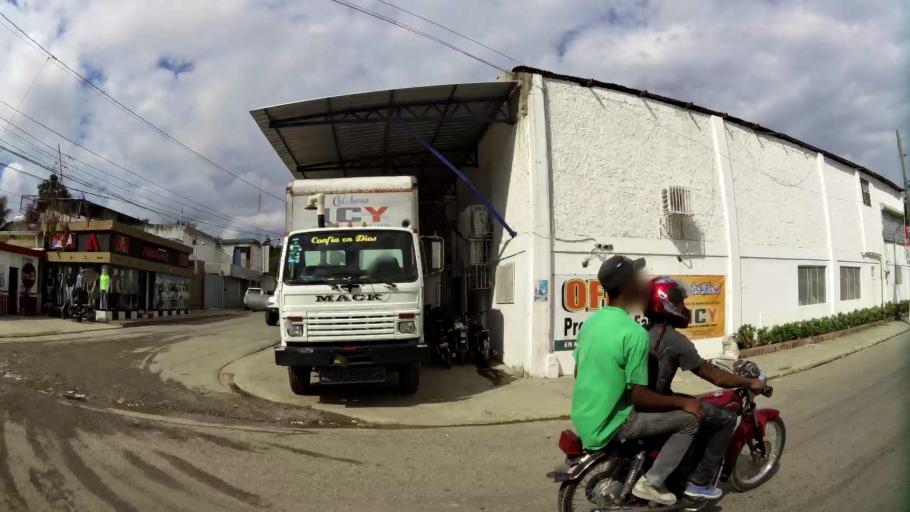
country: DO
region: Santiago
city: Santiago de los Caballeros
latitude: 19.4387
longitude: -70.7055
